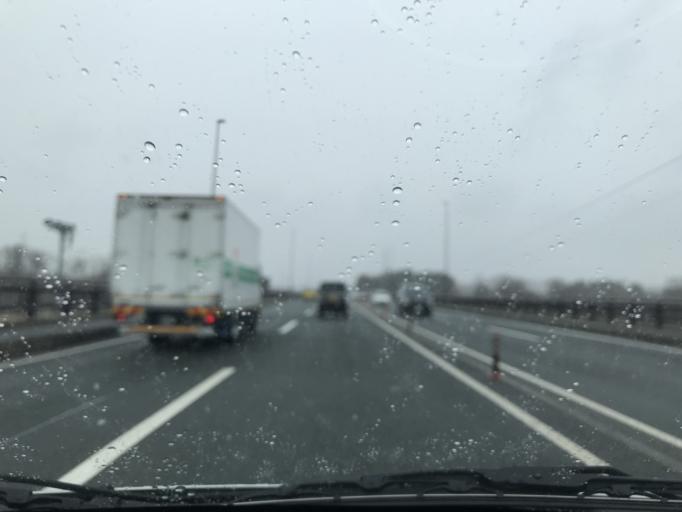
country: JP
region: Iwate
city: Kitakami
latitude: 39.2800
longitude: 141.1022
